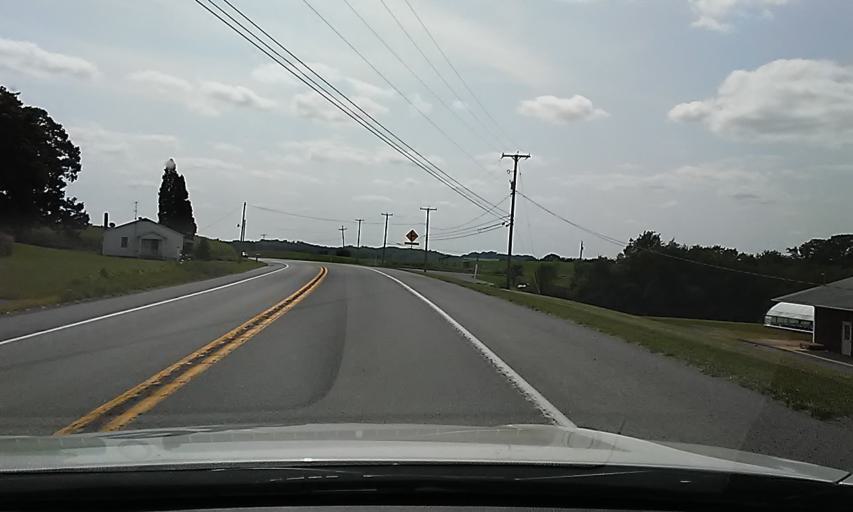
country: US
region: Pennsylvania
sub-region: Jefferson County
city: Punxsutawney
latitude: 40.8994
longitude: -79.0152
